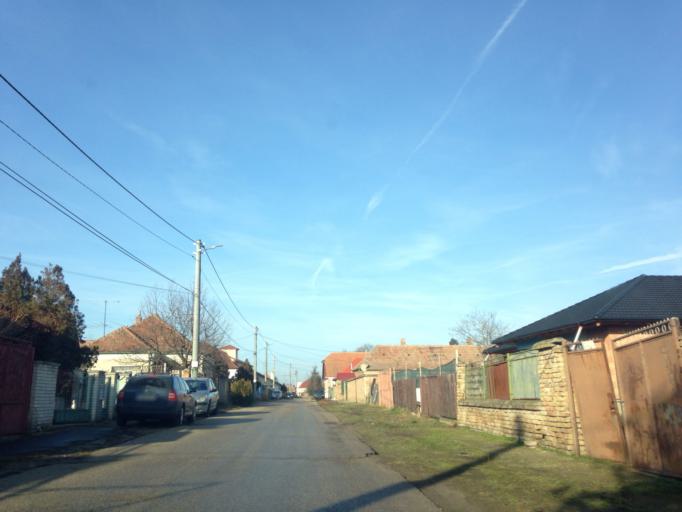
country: SK
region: Nitriansky
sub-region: Okres Nove Zamky
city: Nove Zamky
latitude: 47.9936
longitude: 18.2714
